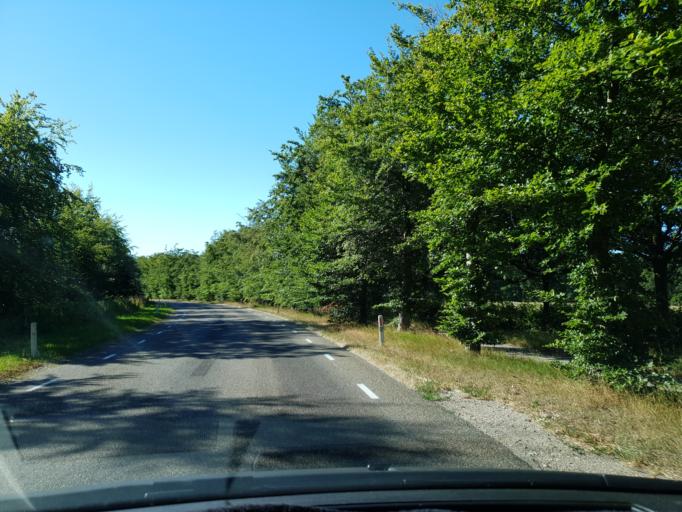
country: NL
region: North Brabant
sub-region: Gemeente Zundert
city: Zundert
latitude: 51.4927
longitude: 4.6067
